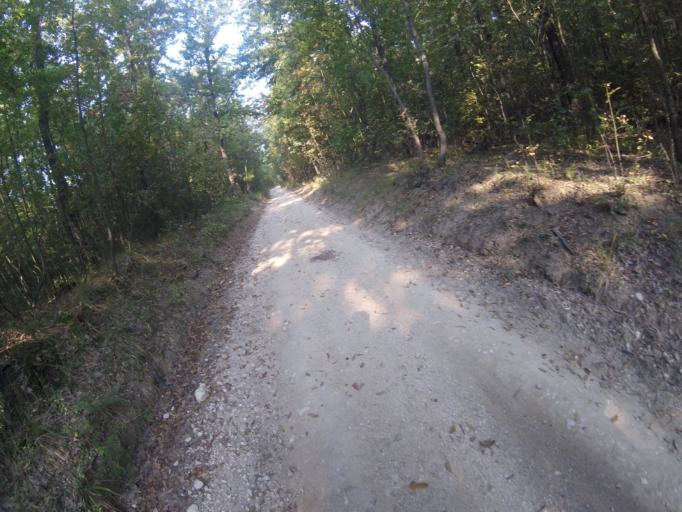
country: HU
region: Pest
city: Pilisszanto
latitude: 47.6778
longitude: 18.8722
